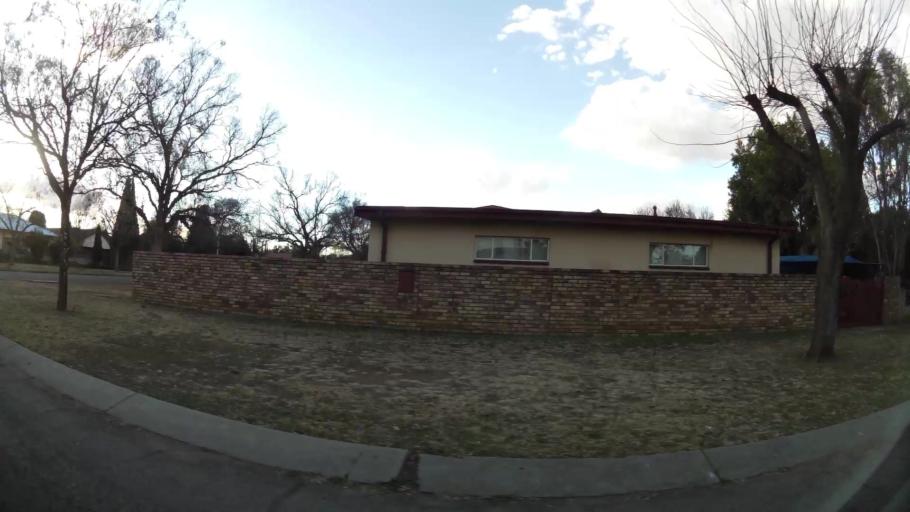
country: ZA
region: North-West
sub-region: Dr Kenneth Kaunda District Municipality
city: Potchefstroom
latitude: -26.7374
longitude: 27.0910
